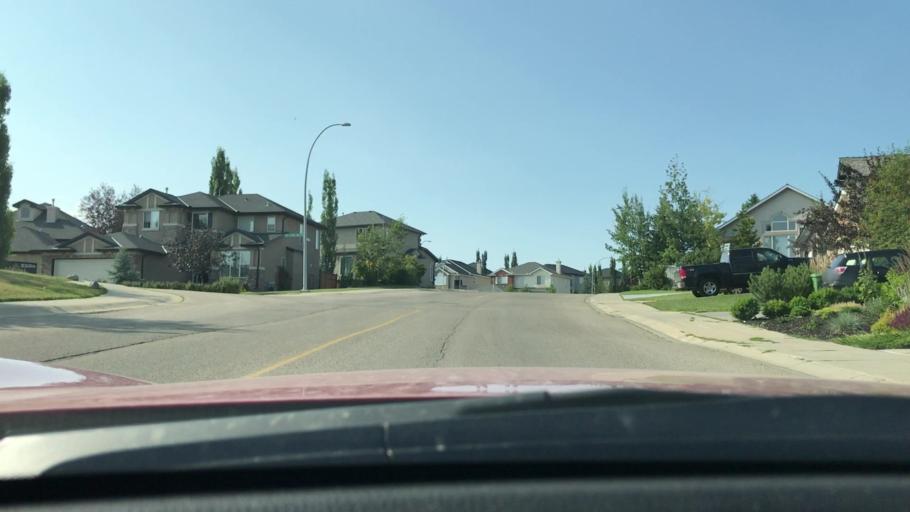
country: CA
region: Alberta
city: Calgary
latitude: 51.0281
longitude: -114.1820
